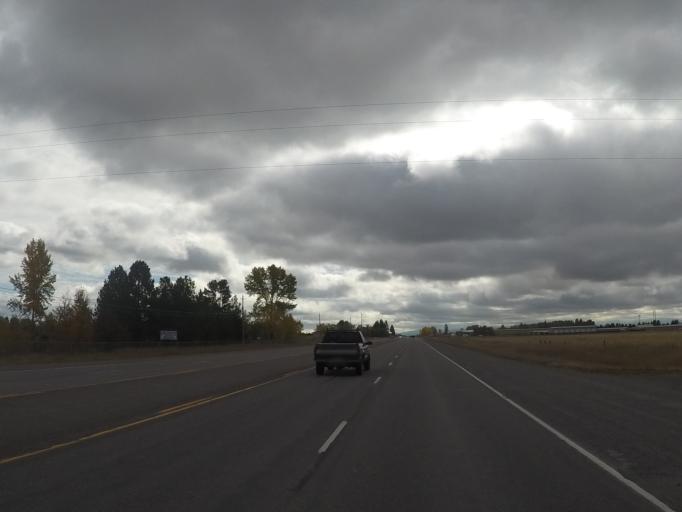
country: US
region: Montana
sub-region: Flathead County
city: Columbia Falls
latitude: 48.3673
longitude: -114.2410
